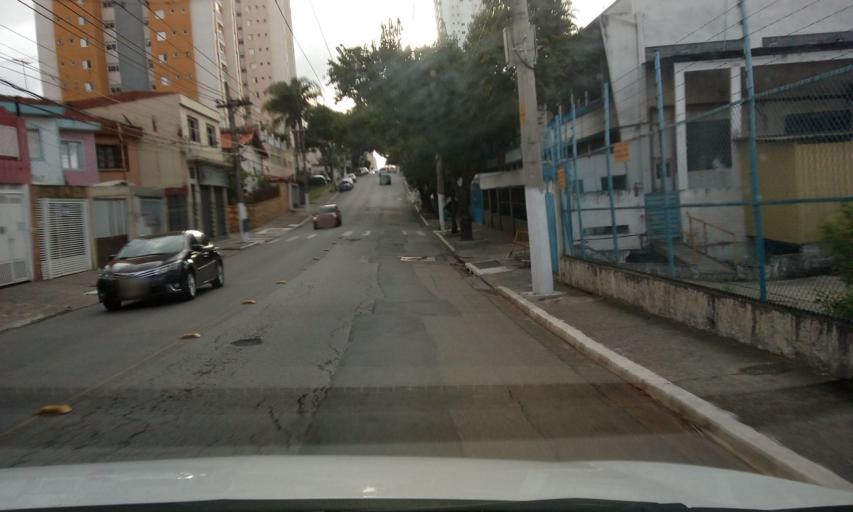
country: BR
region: Sao Paulo
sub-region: Sao Caetano Do Sul
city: Sao Caetano do Sul
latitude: -23.5430
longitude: -46.5525
